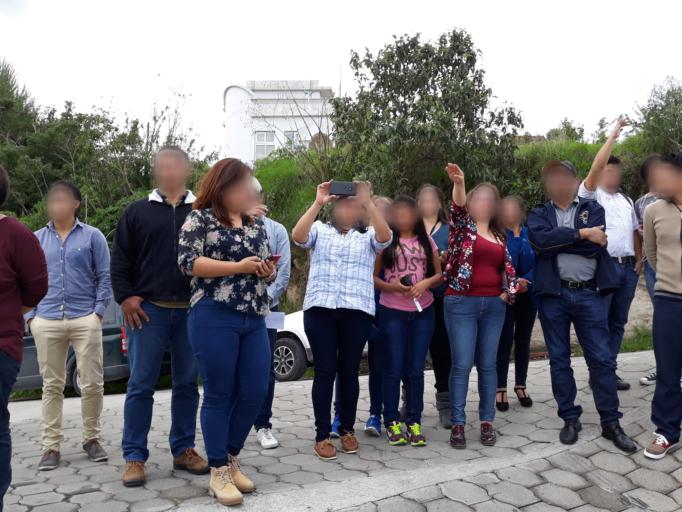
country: GT
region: Quetzaltenango
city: Salcaja
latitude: 14.8776
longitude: -91.4498
